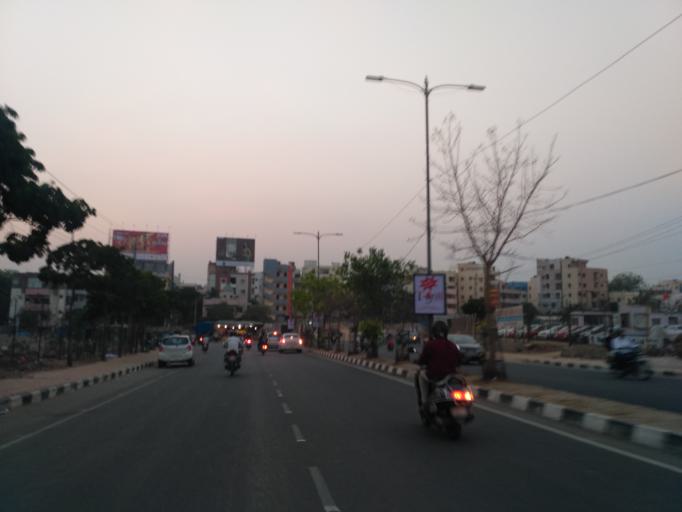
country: IN
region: Telangana
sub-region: Rangareddi
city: Kukatpalli
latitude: 17.4429
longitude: 78.3944
